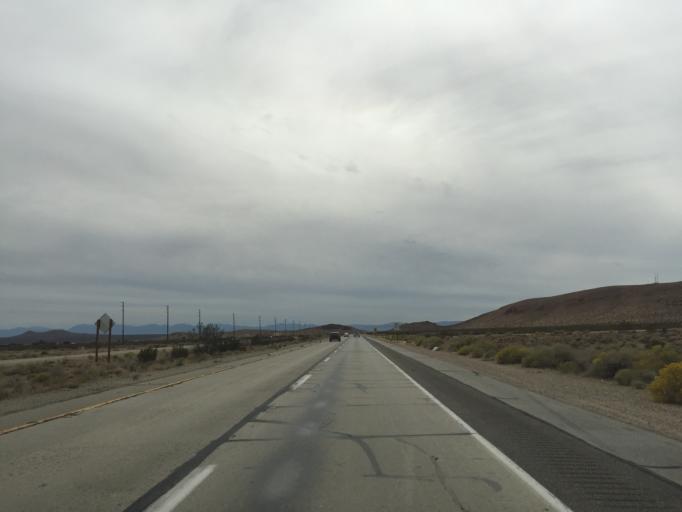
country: US
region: California
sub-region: Kern County
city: Mojave
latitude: 34.9941
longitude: -118.1599
